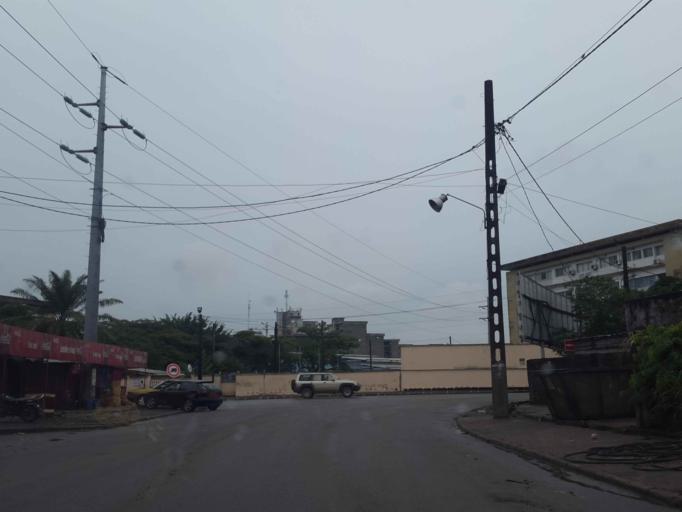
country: CM
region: Littoral
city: Douala
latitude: 4.0336
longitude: 9.6923
